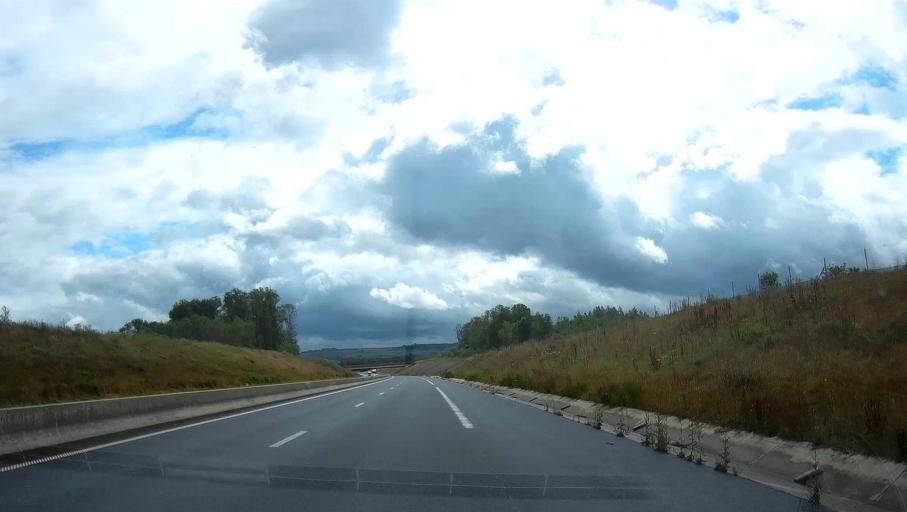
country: FR
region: Champagne-Ardenne
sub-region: Departement des Ardennes
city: Rimogne
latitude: 49.8191
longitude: 4.5146
